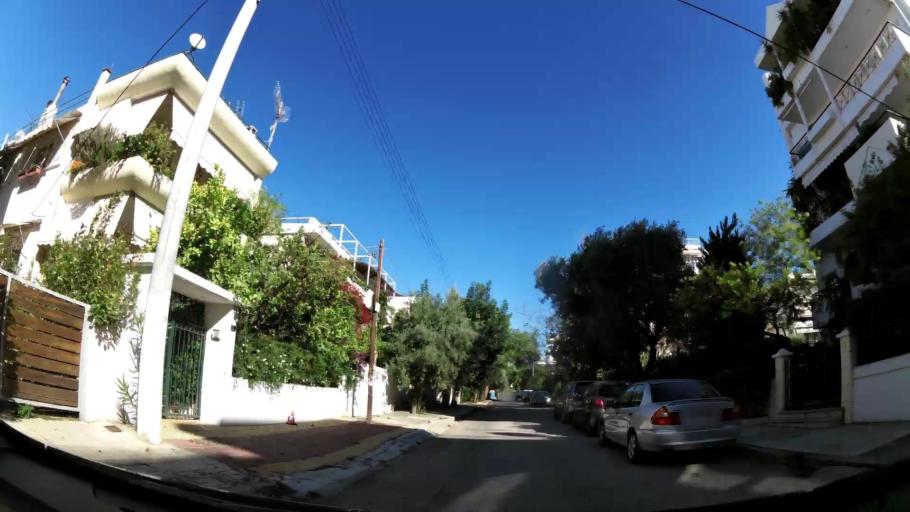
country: GR
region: Attica
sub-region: Nomarchia Athinas
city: Glyfada
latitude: 37.8529
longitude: 23.7576
